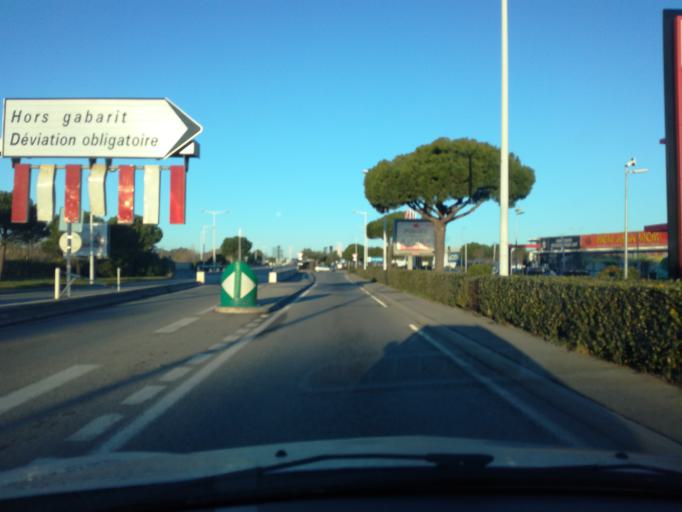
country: FR
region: Provence-Alpes-Cote d'Azur
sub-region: Departement du Var
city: Frejus
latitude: 43.4367
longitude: 6.7216
